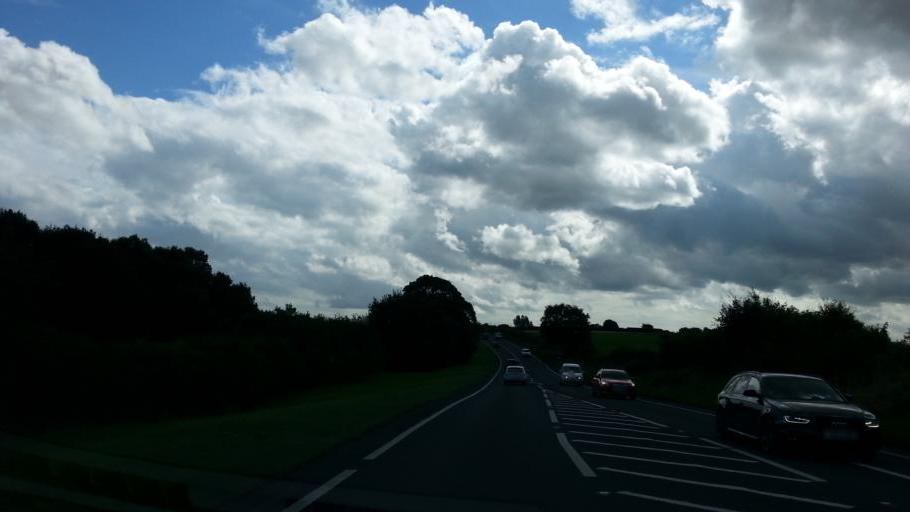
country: GB
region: England
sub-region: Nottinghamshire
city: Bilsthorpe
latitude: 53.1251
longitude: -1.0575
